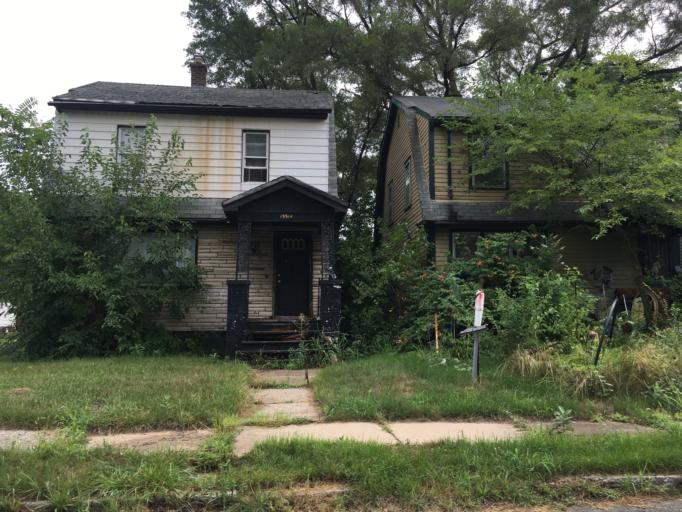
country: US
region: Michigan
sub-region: Wayne County
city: Highland Park
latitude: 42.4060
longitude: -83.1545
